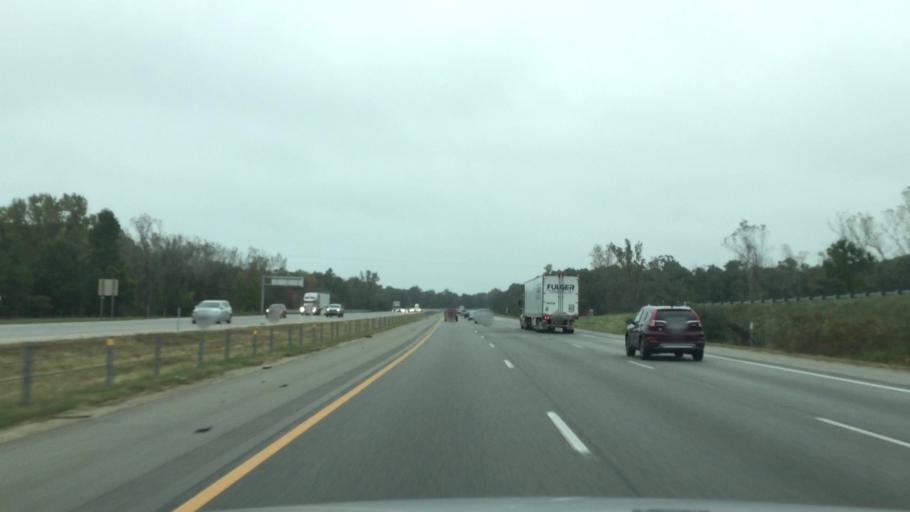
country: US
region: Michigan
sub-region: Berrien County
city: Stevensville
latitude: 42.0120
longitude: -86.5325
